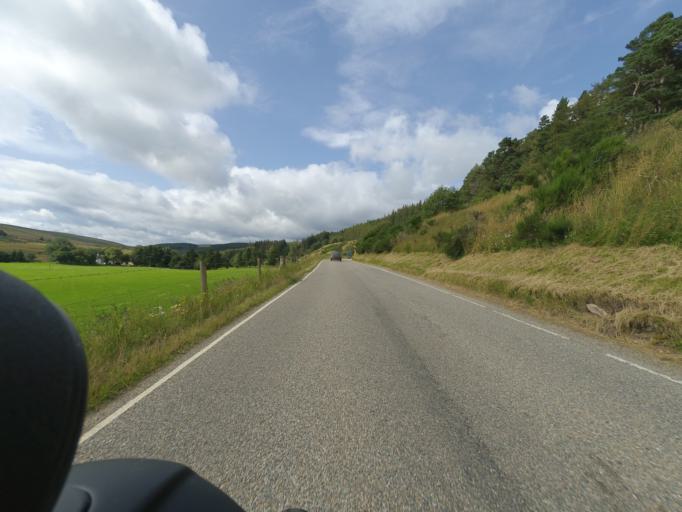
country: GB
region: Scotland
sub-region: Highland
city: Grantown on Spey
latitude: 57.2580
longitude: -3.3897
